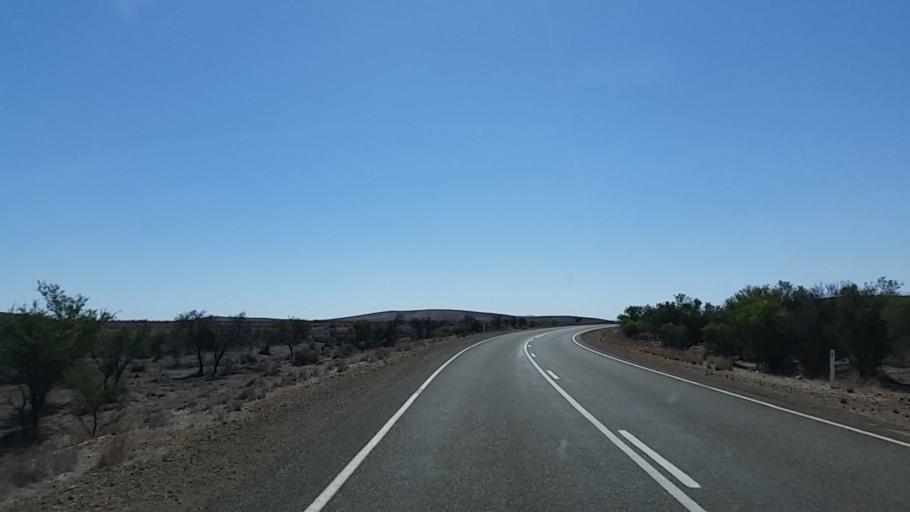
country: AU
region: South Australia
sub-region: Flinders Ranges
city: Quorn
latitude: -32.1512
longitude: 138.5234
